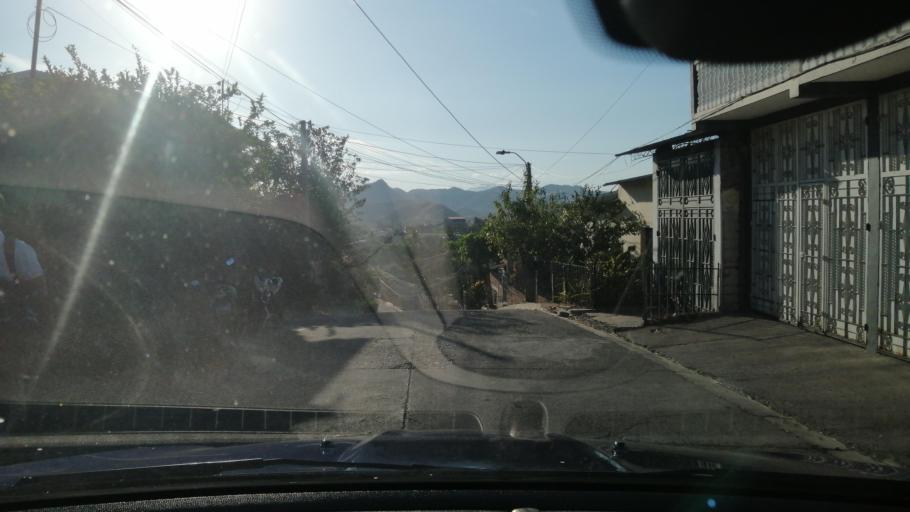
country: SV
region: Santa Ana
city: Metapan
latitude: 14.3318
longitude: -89.4387
